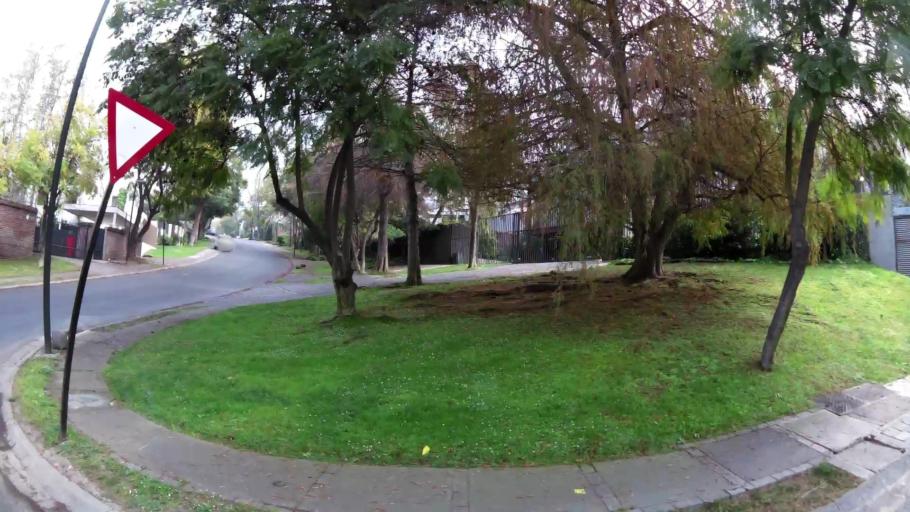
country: CL
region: Santiago Metropolitan
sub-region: Provincia de Santiago
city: Villa Presidente Frei, Nunoa, Santiago, Chile
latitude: -33.3682
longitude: -70.5724
